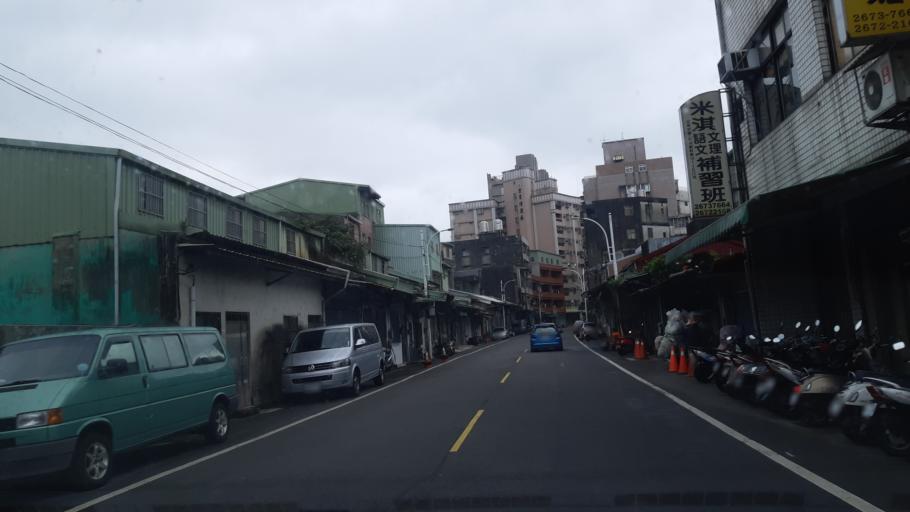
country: TW
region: Taiwan
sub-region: Taoyuan
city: Taoyuan
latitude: 24.9296
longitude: 121.3696
